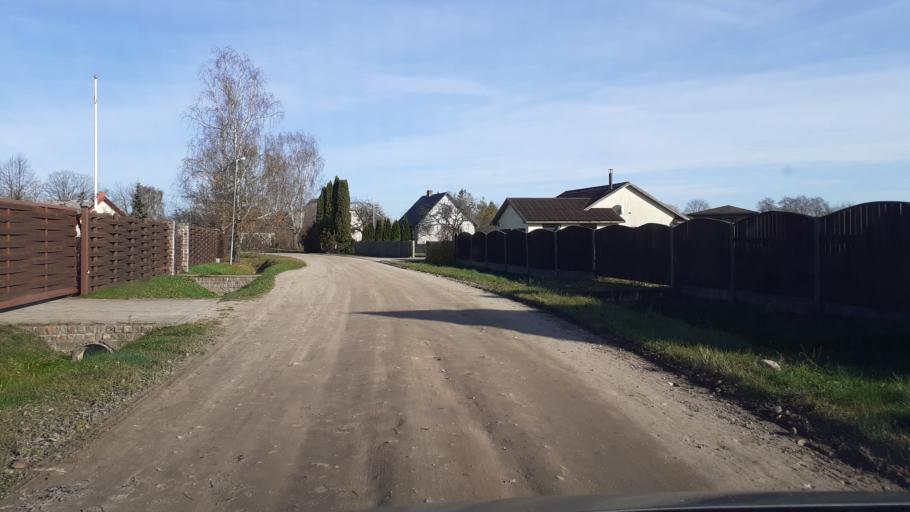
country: LV
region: Kuldigas Rajons
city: Kuldiga
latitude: 56.9584
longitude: 21.9965
